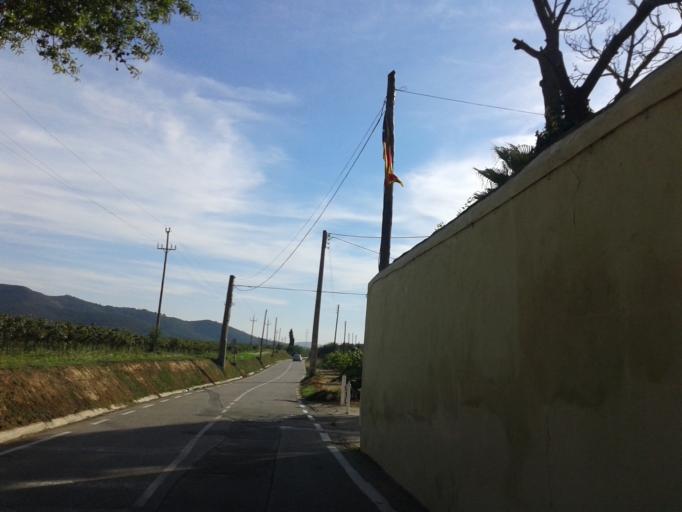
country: ES
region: Catalonia
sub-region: Provincia de Barcelona
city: La Granada
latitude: 41.3469
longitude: 1.7376
